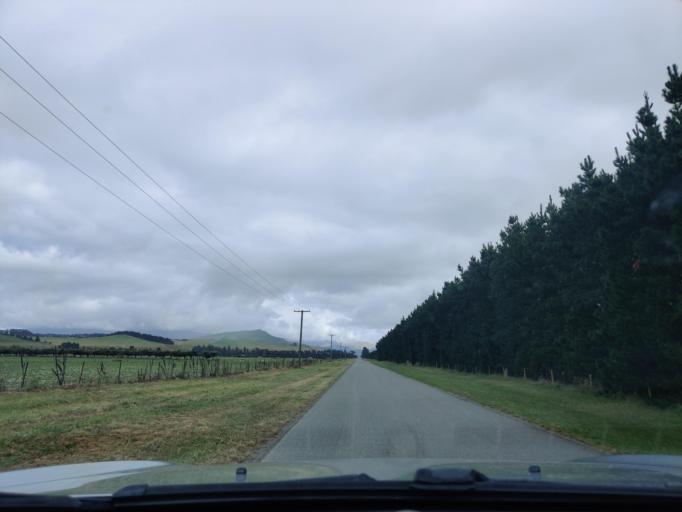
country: NZ
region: Canterbury
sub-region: Hurunui District
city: Amberley
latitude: -43.0753
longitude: 172.6897
